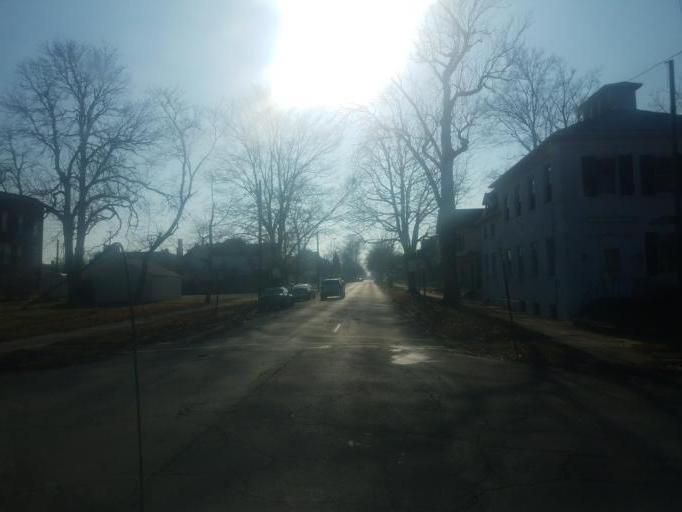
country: US
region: Ohio
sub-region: Seneca County
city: Tiffin
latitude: 41.1133
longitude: -83.1780
